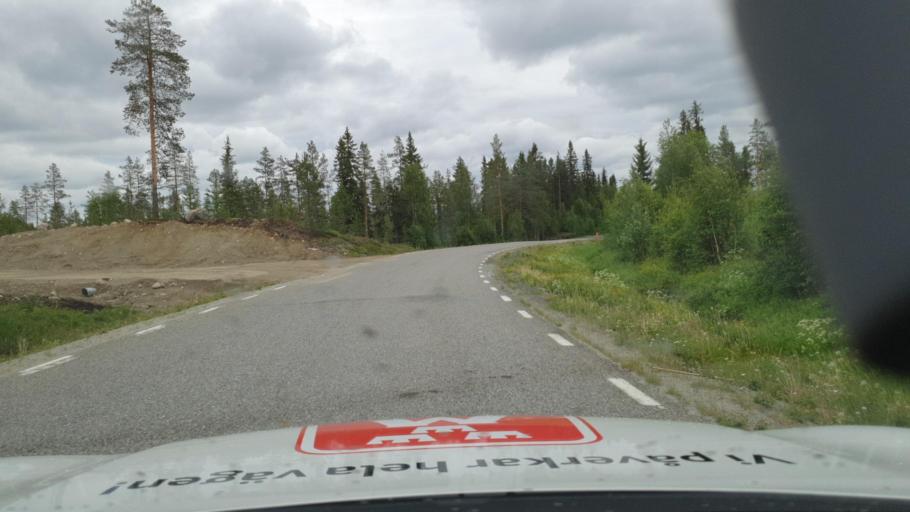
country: SE
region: Vaesterbotten
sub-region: Lycksele Kommun
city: Lycksele
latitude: 64.2505
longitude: 18.2159
